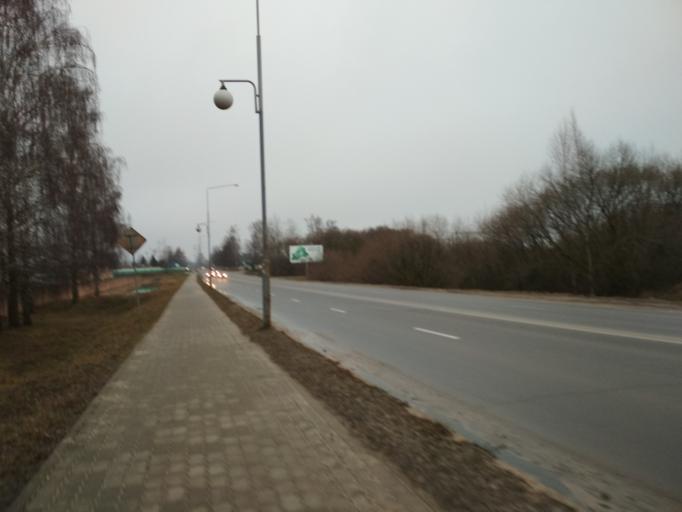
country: BY
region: Minsk
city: Mar''ina Horka
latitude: 53.5035
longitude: 28.1481
